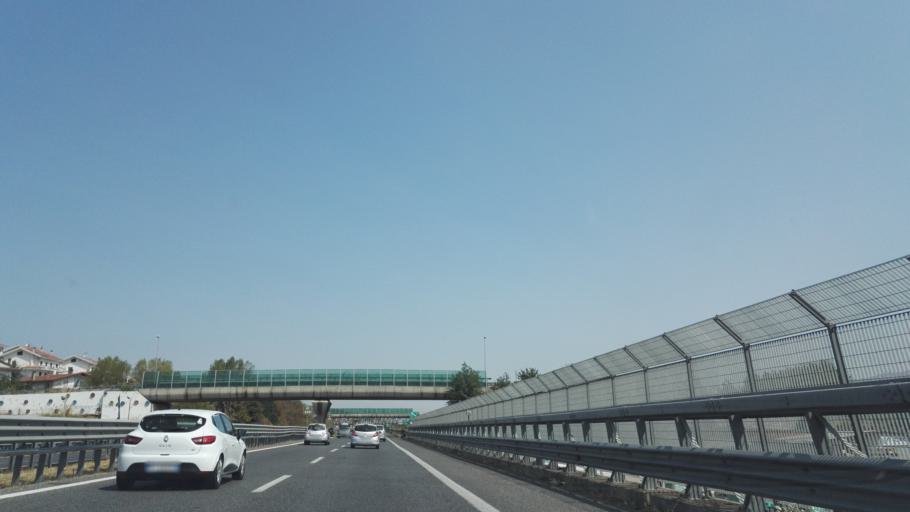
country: IT
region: Calabria
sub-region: Provincia di Cosenza
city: Settimo
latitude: 39.3702
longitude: 16.2366
